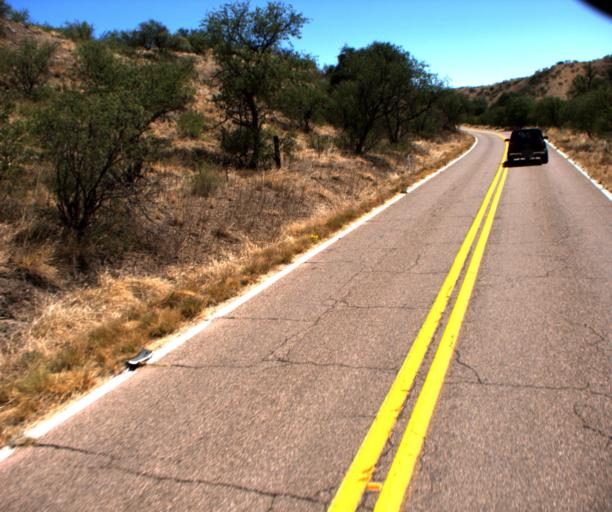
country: US
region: Arizona
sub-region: Santa Cruz County
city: Rio Rico
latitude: 31.3975
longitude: -111.0337
